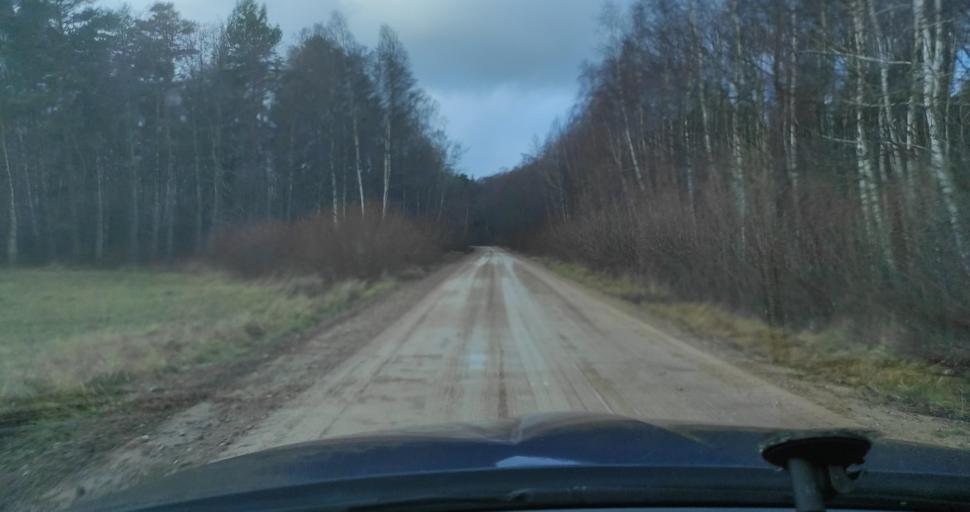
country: LV
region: Pavilostas
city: Pavilosta
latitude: 56.8553
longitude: 21.1274
